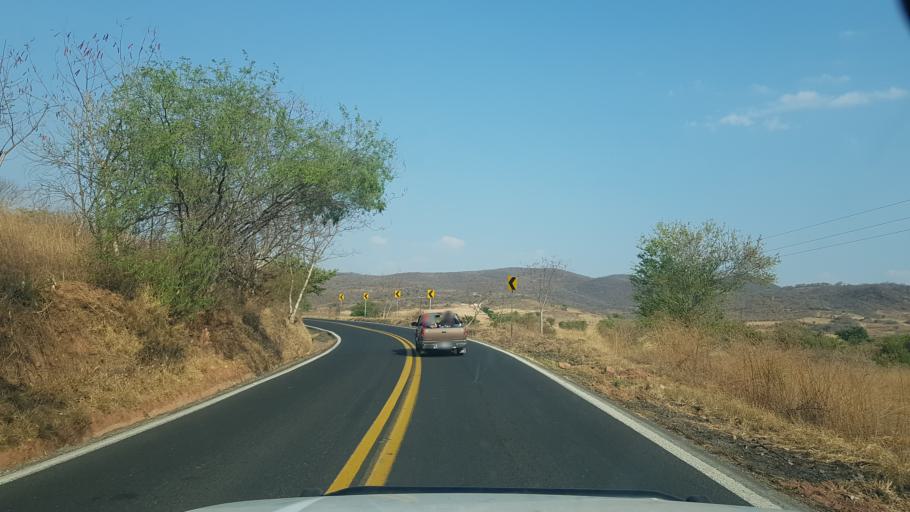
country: MX
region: Puebla
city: Calmeca
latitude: 18.6418
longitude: -98.6194
